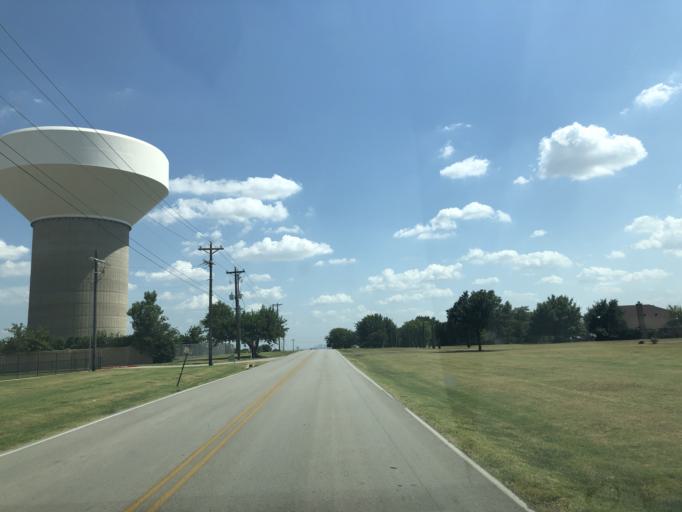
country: US
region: Texas
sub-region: Tarrant County
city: Haslet
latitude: 32.9273
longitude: -97.3316
